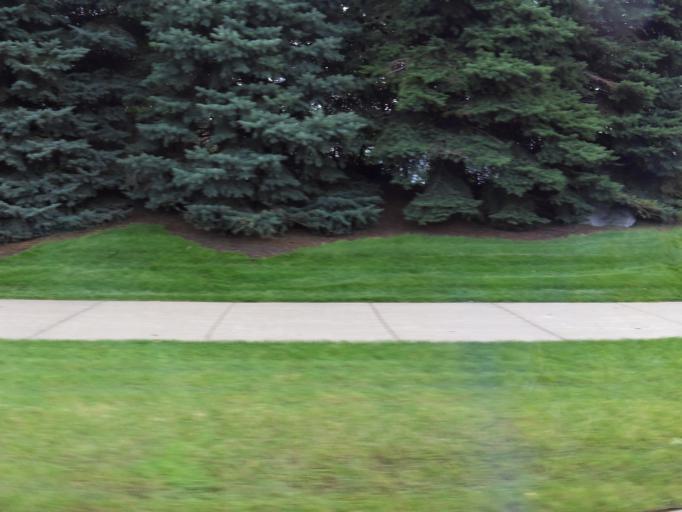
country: US
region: Minnesota
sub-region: Dakota County
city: Inver Grove Heights
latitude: 44.8250
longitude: -93.0417
